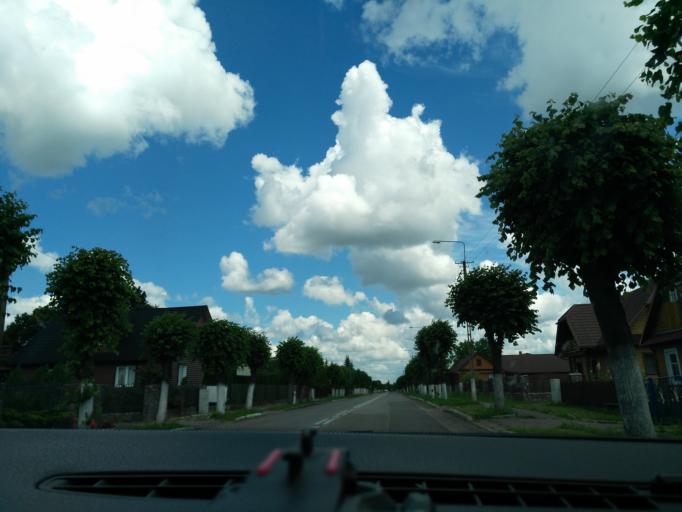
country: PL
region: Podlasie
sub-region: Powiat bielski
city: Bielsk Podlaski
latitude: 52.8044
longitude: 23.1932
